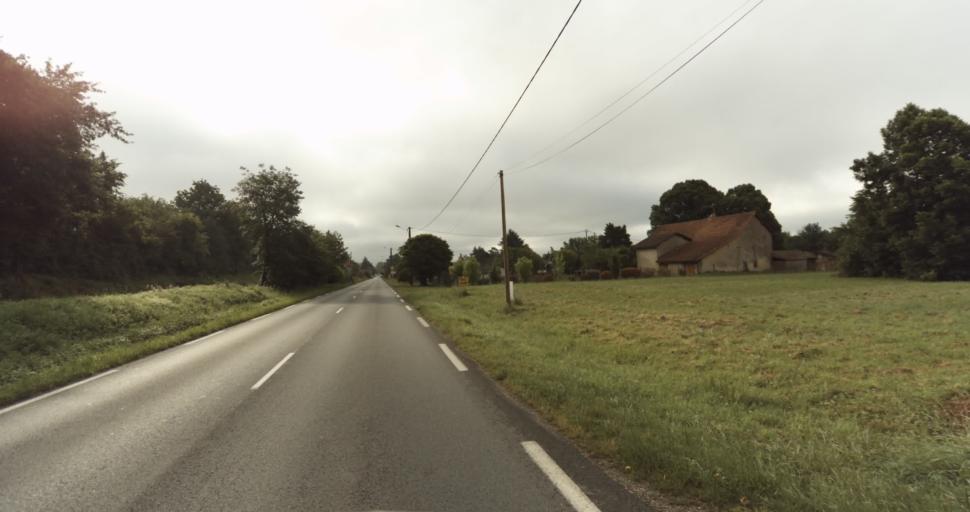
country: FR
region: Aquitaine
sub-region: Departement de la Dordogne
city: Mouleydier
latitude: 44.8505
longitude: 0.6205
